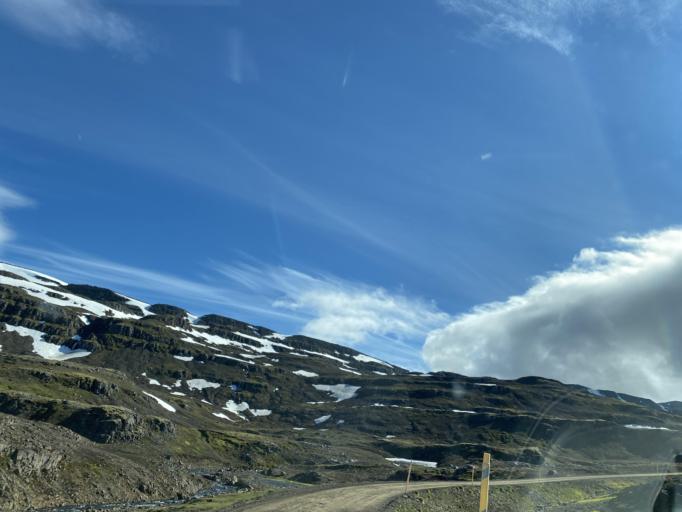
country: IS
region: East
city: Eskifjoerdur
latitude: 65.1704
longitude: -14.1208
